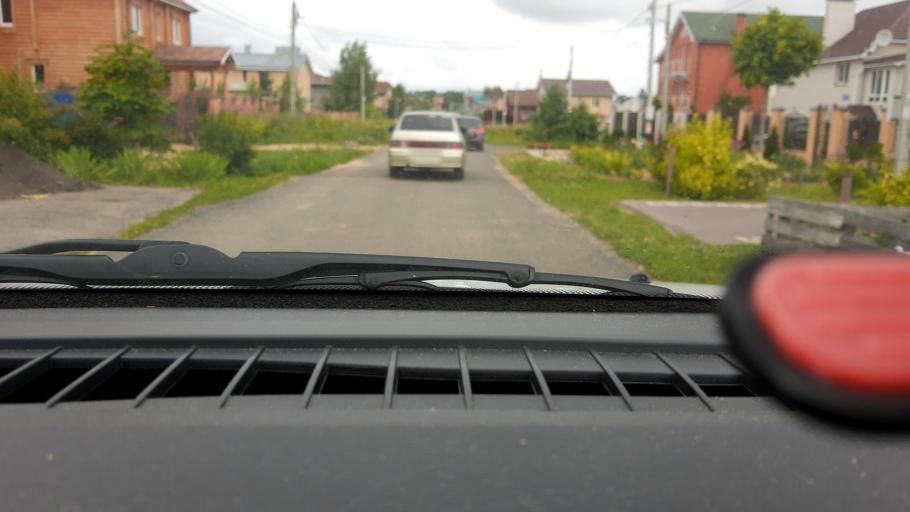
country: RU
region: Nizjnij Novgorod
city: Nizhniy Novgorod
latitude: 56.2165
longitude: 43.9607
